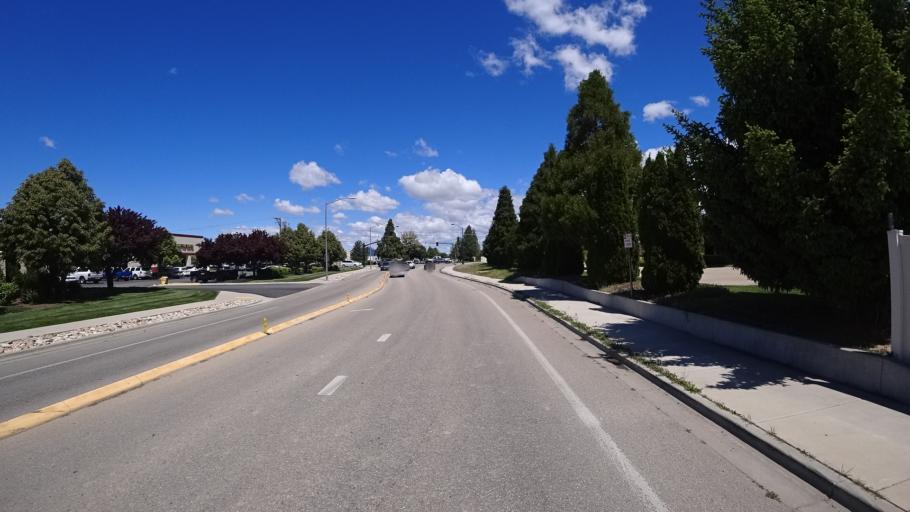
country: US
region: Idaho
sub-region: Ada County
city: Meridian
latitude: 43.6329
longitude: -116.3495
